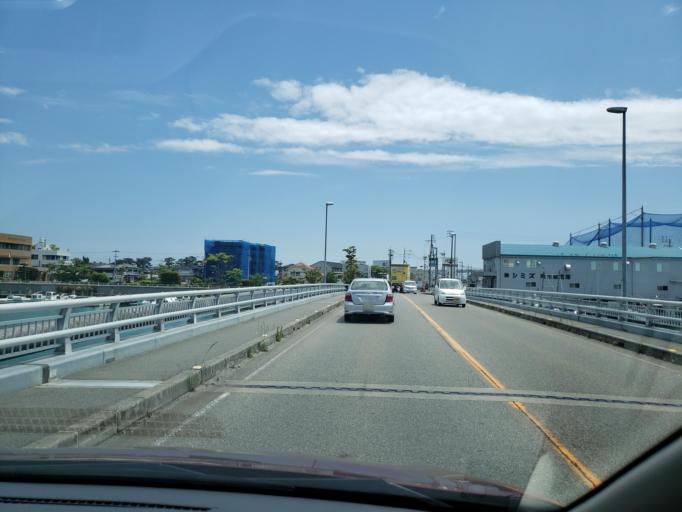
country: JP
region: Tokushima
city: Tokushima-shi
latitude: 34.0600
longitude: 134.5797
